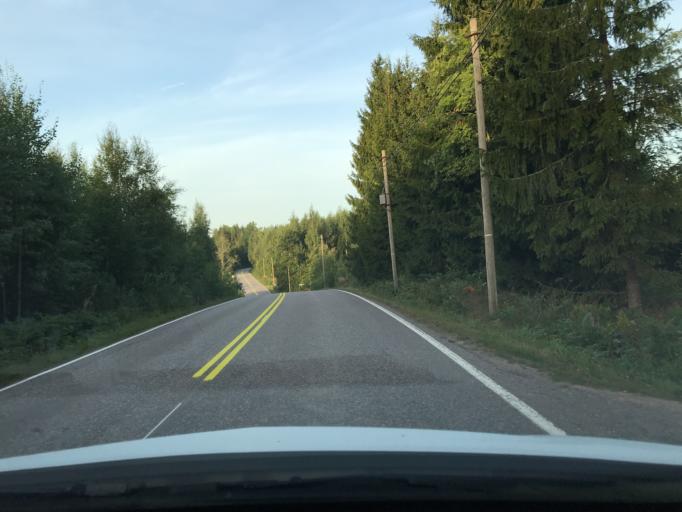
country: FI
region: Uusimaa
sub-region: Helsinki
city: Vihti
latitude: 60.4253
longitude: 24.5122
